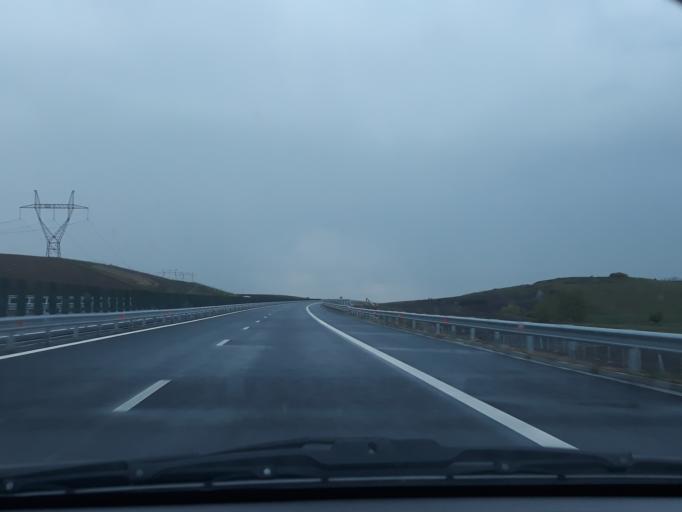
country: RO
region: Mures
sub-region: Comuna Sanpaul
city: Sanpaul
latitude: 46.4394
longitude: 24.3393
